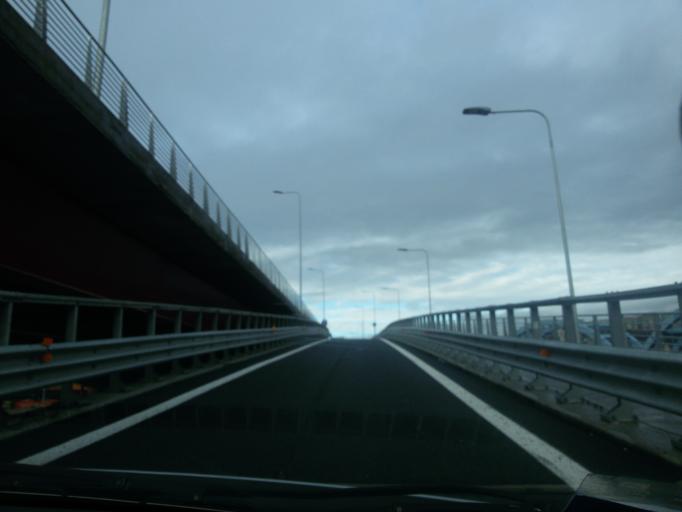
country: IT
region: Liguria
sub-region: Provincia di Genova
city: San Teodoro
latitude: 44.4118
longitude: 8.8797
